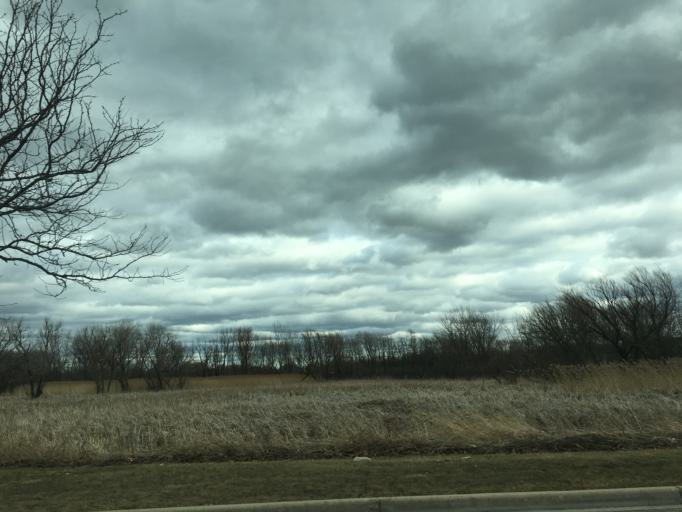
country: US
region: Illinois
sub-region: Cook County
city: Schaumburg
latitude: 42.0449
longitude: -88.1200
